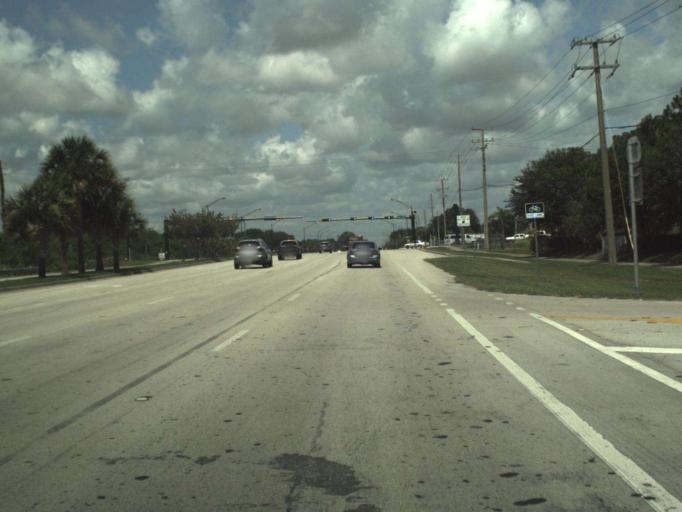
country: US
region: Florida
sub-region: Indian River County
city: West Vero Corridor
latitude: 27.6392
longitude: -80.4616
